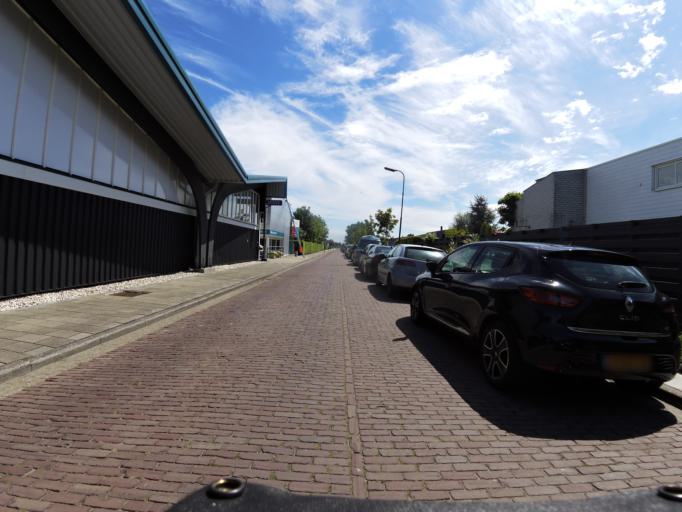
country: NL
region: Zeeland
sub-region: Gemeente Goes
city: Goes
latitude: 51.5531
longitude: 3.8092
